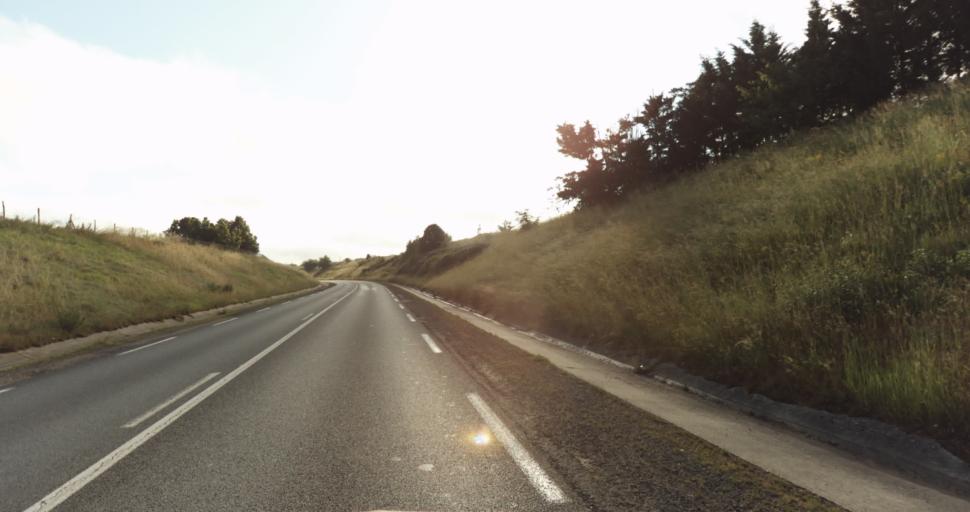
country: FR
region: Aquitaine
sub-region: Departement de la Dordogne
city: Cours-de-Pile
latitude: 44.8309
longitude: 0.5227
